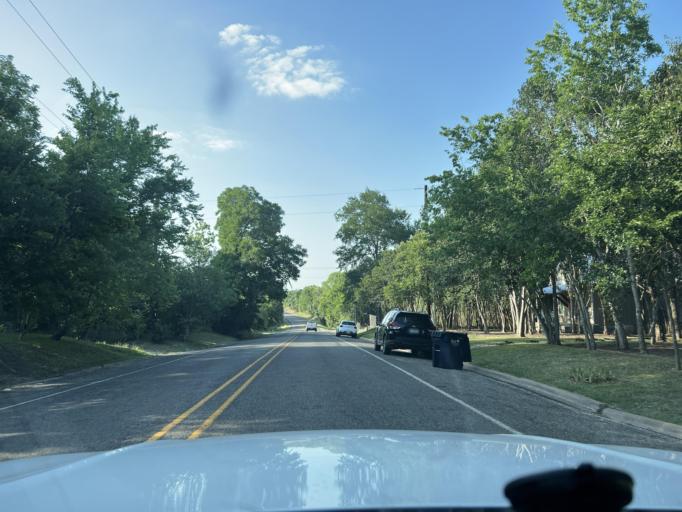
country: US
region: Texas
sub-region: Washington County
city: Brenham
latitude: 30.1448
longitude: -96.2571
